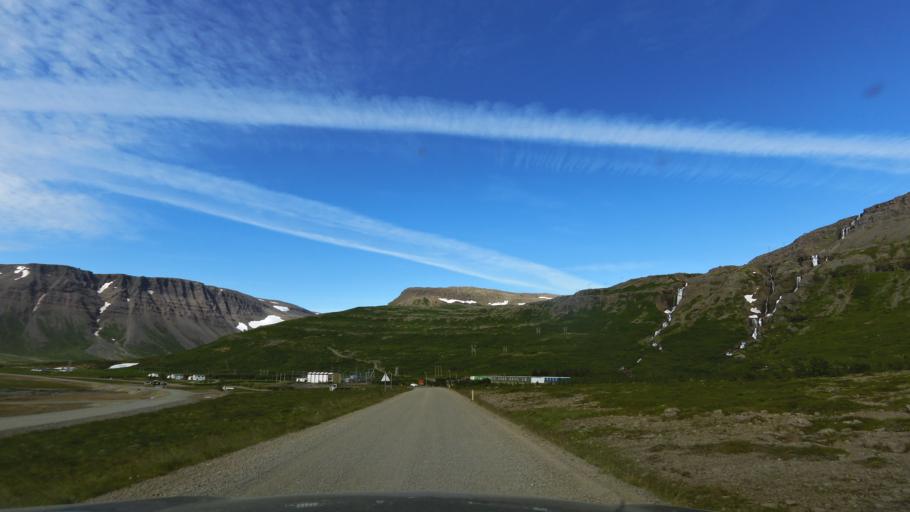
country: IS
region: Westfjords
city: Isafjoerdur
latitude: 65.7716
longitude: -23.1706
